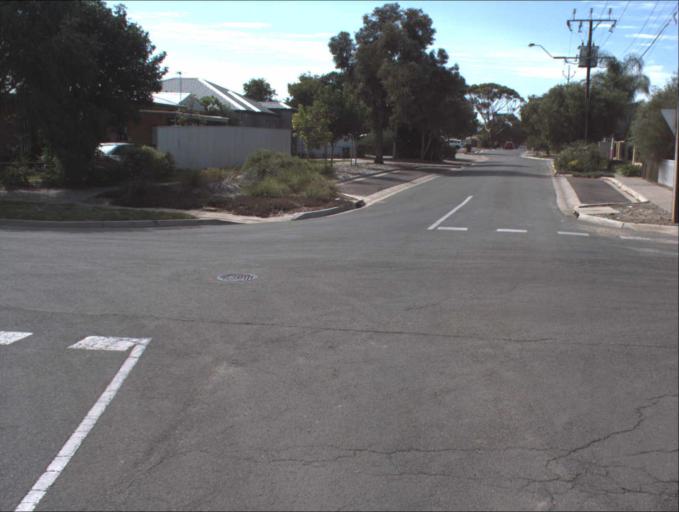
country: AU
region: South Australia
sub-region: Port Adelaide Enfield
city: Klemzig
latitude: -34.8725
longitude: 138.6417
